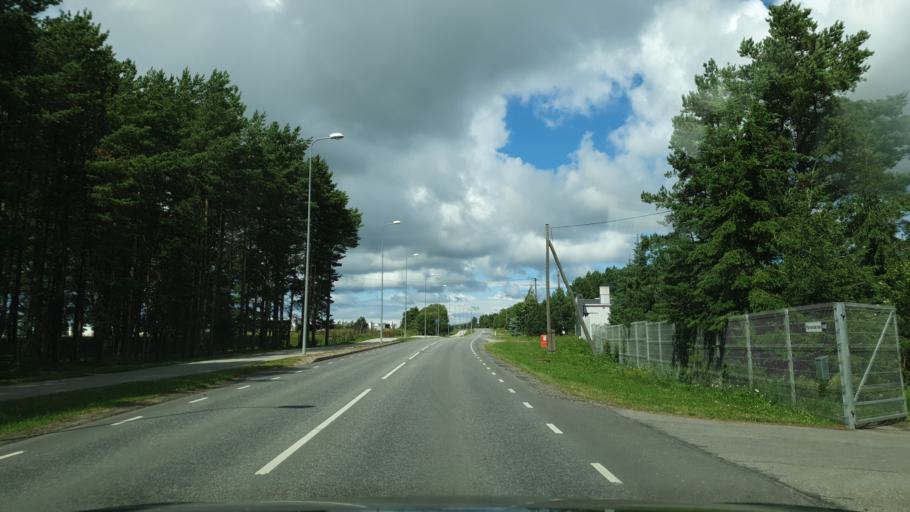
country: EE
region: Harju
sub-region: Viimsi vald
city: Viimsi
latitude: 59.4964
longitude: 24.8741
